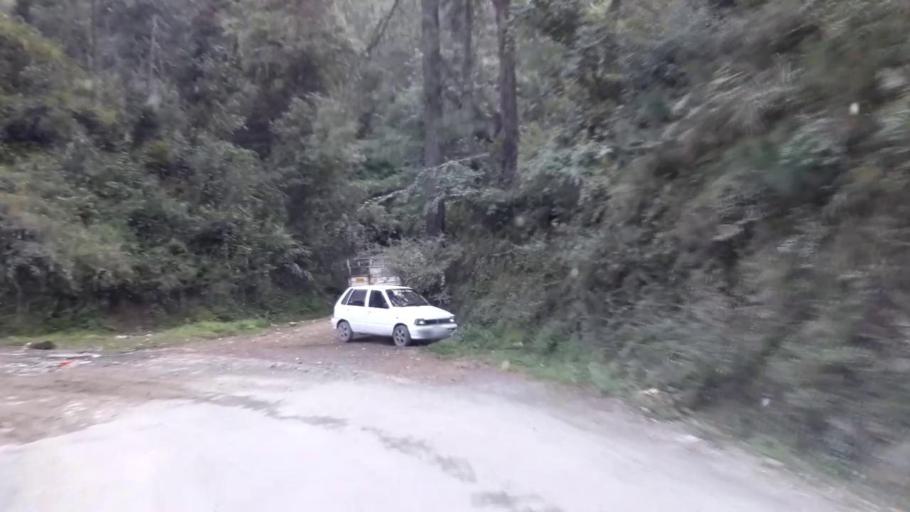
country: IN
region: Himachal Pradesh
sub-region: Shimla
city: Shimla
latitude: 31.0652
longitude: 77.1480
